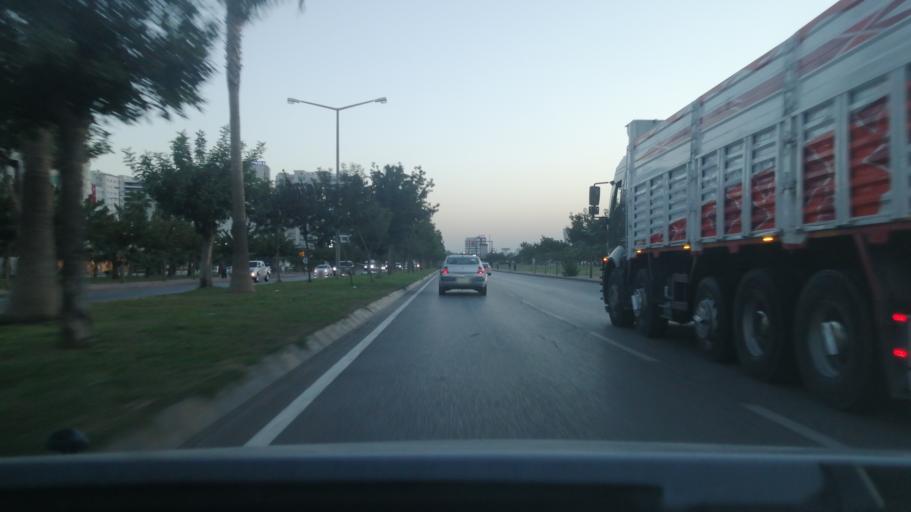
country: TR
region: Adana
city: Seyhan
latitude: 37.0217
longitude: 35.2531
